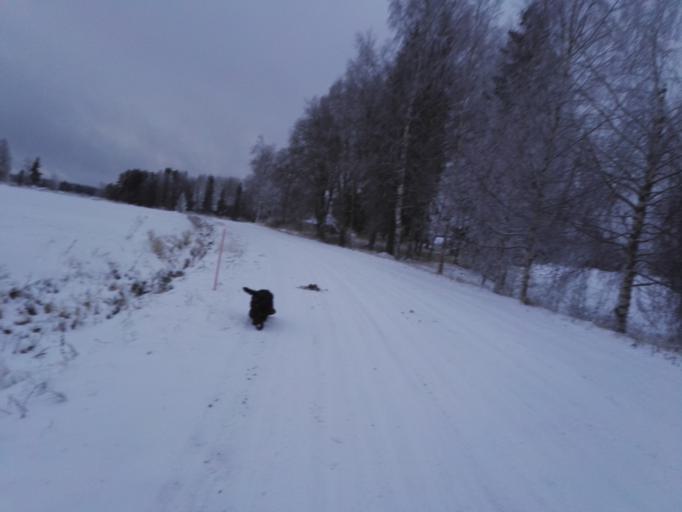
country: FI
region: Satakunta
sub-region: Pohjois-Satakunta
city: Jaemijaervi
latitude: 61.7829
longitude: 22.8778
